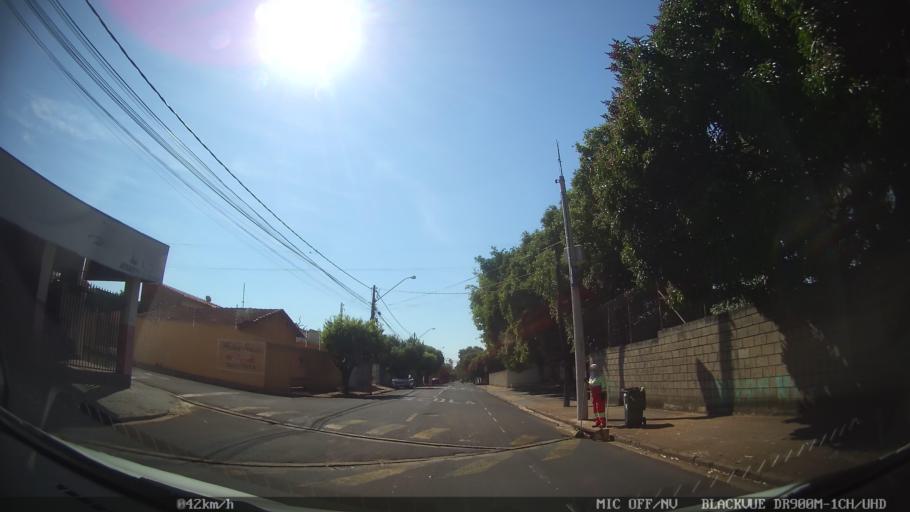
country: BR
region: Sao Paulo
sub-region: Sao Jose Do Rio Preto
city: Sao Jose do Rio Preto
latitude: -20.7741
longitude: -49.4181
